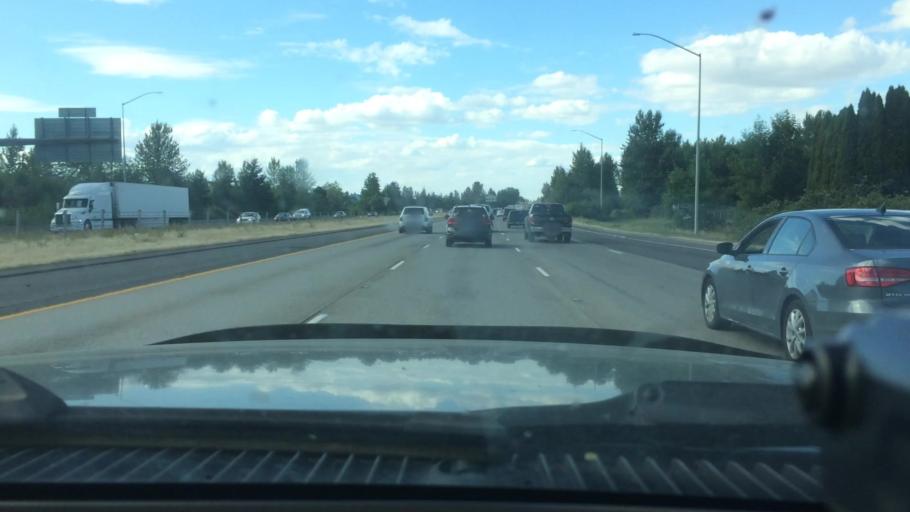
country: US
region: Oregon
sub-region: Marion County
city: Four Corners
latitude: 44.9200
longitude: -122.9897
